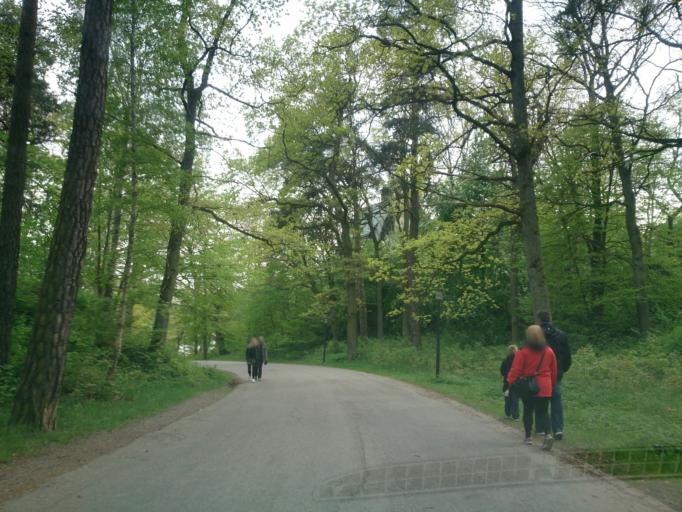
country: SE
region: Stockholm
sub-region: Stockholms Kommun
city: OEstermalm
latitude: 59.3254
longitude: 18.1106
